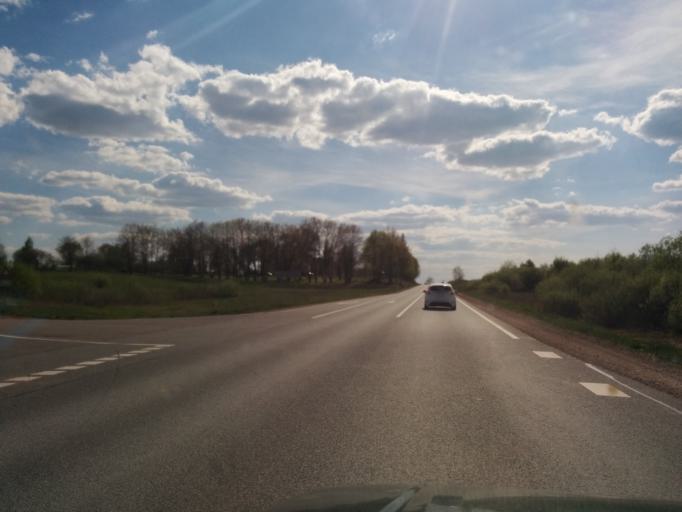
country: LV
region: Sigulda
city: Sigulda
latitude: 57.2626
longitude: 24.8749
